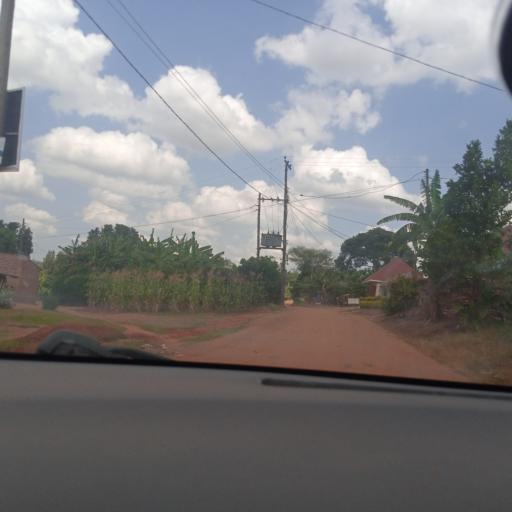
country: UG
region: Central Region
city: Masaka
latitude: -0.3268
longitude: 31.7423
